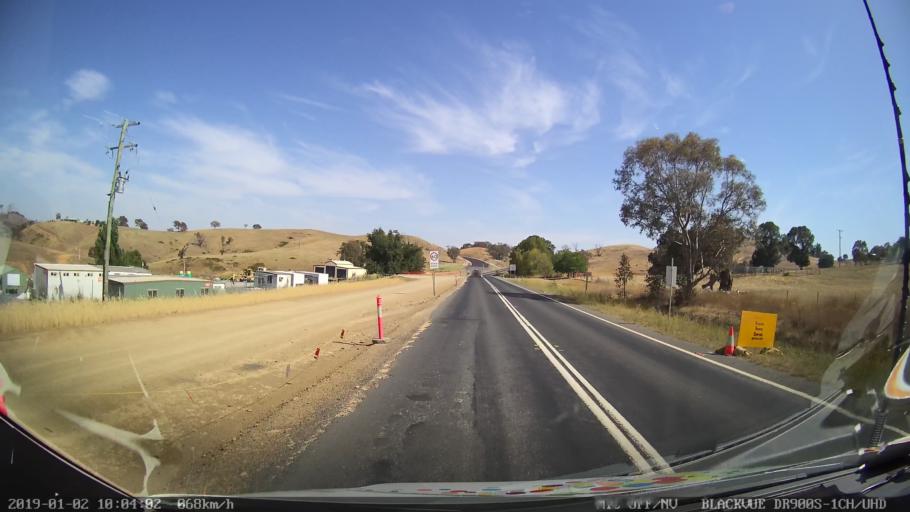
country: AU
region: New South Wales
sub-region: Gundagai
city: Gundagai
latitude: -35.1717
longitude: 148.1242
